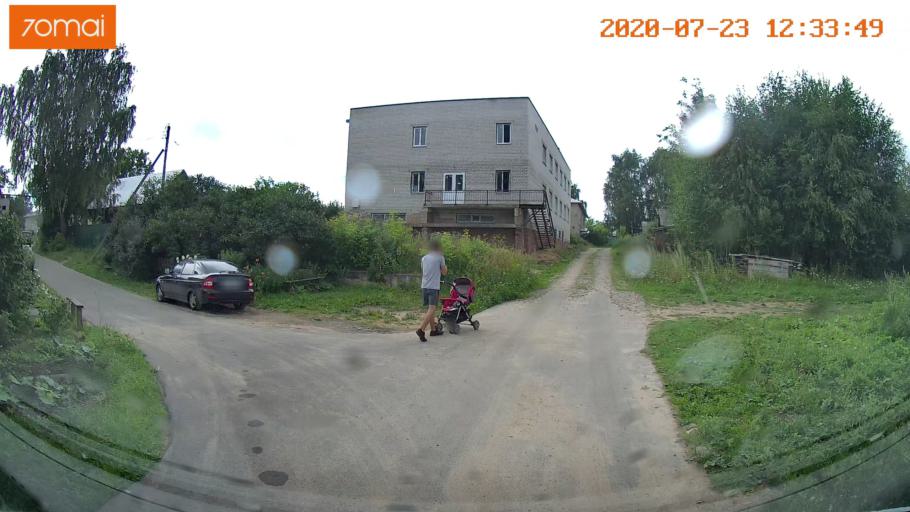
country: RU
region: Ivanovo
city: Bogorodskoye
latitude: 57.0495
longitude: 41.0086
